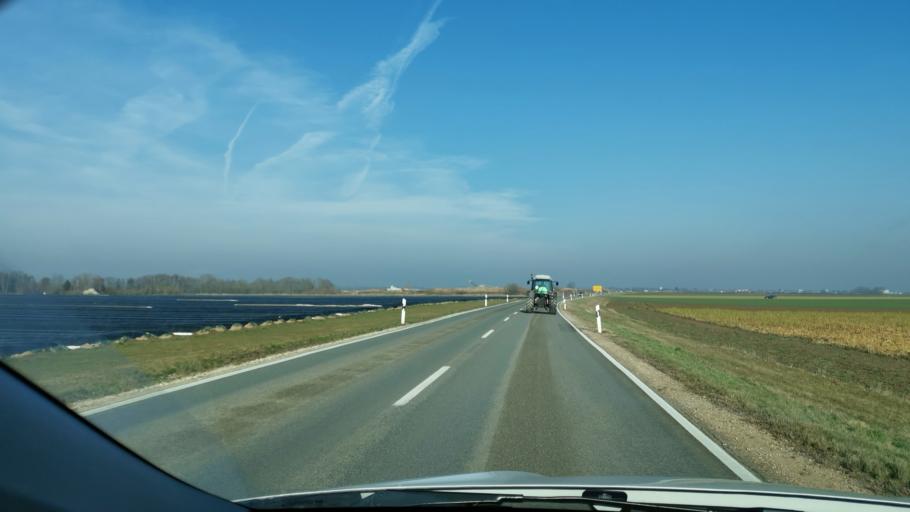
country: DE
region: Bavaria
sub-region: Swabia
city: Munster
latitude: 48.6571
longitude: 10.9208
